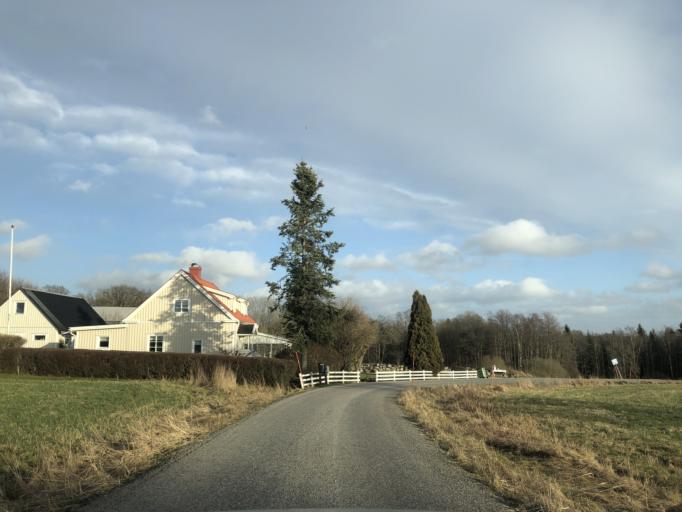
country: SE
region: Vaestra Goetaland
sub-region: Ulricehamns Kommun
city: Ulricehamn
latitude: 57.8081
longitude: 13.3646
